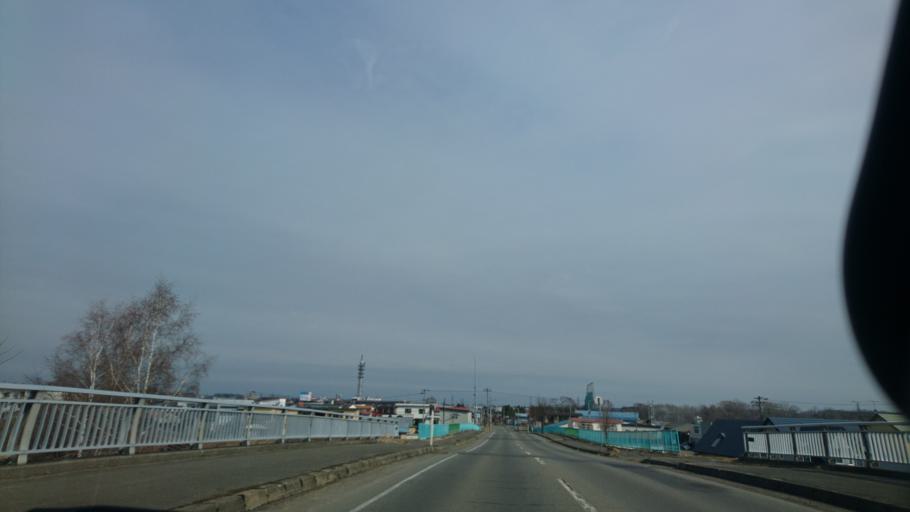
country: JP
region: Hokkaido
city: Obihiro
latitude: 42.9492
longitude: 143.2075
